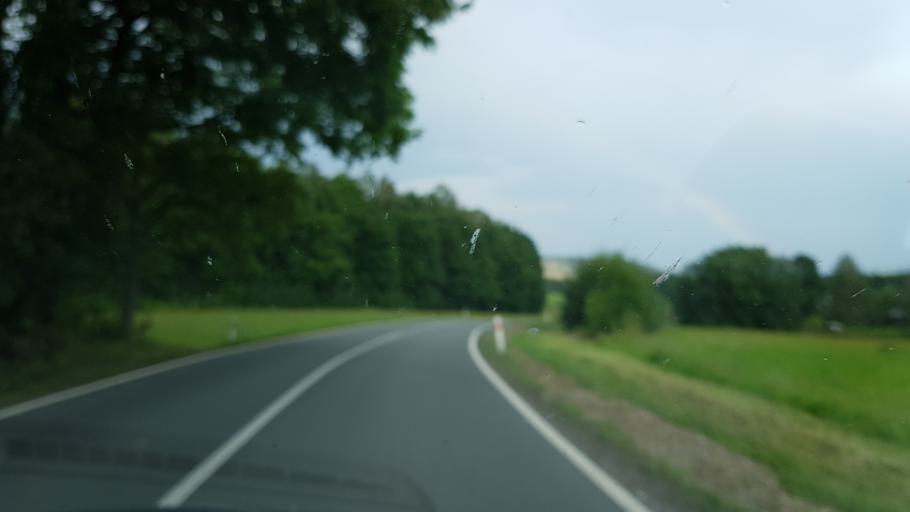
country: CZ
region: Pardubicky
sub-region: Okres Usti nad Orlici
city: Kraliky
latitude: 50.1030
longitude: 16.7893
